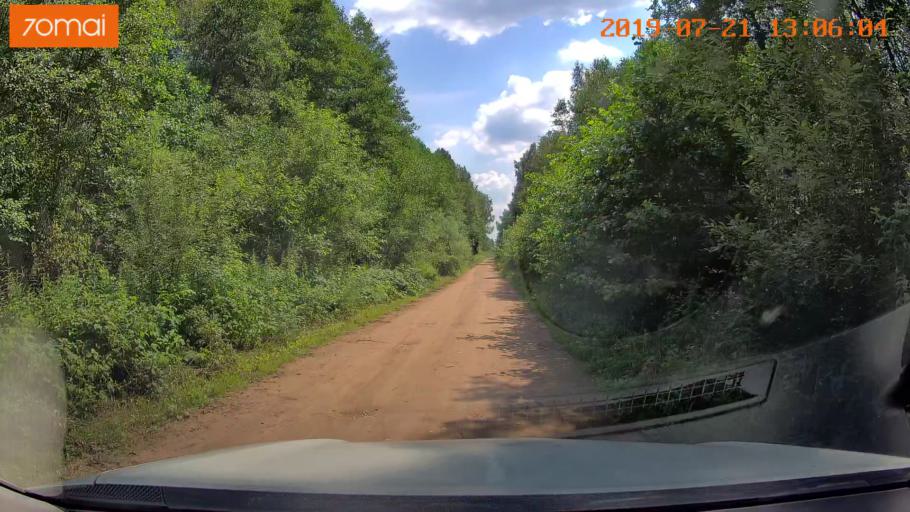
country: BY
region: Grodnenskaya
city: Lyubcha
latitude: 53.8302
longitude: 26.0401
